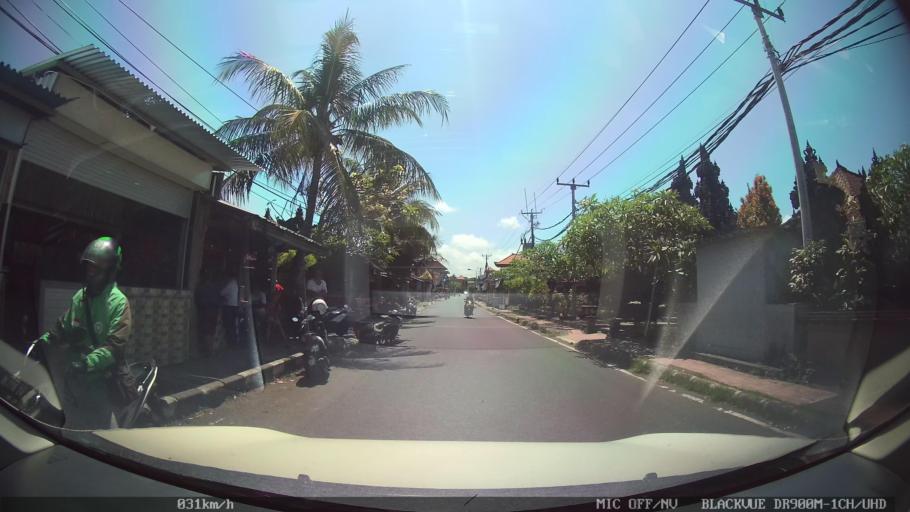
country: ID
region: Bali
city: Klungkung
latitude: -8.5792
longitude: 115.3549
